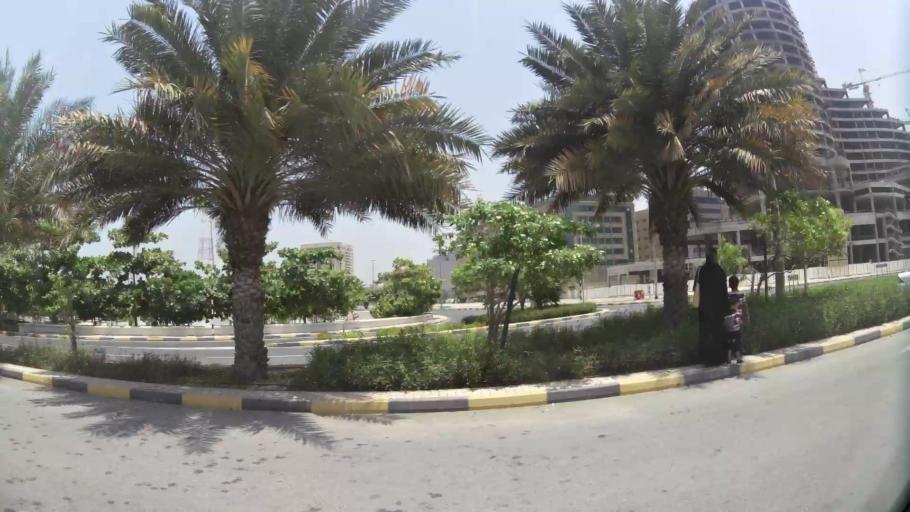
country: AE
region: Ash Shariqah
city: Sharjah
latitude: 25.3312
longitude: 55.3601
